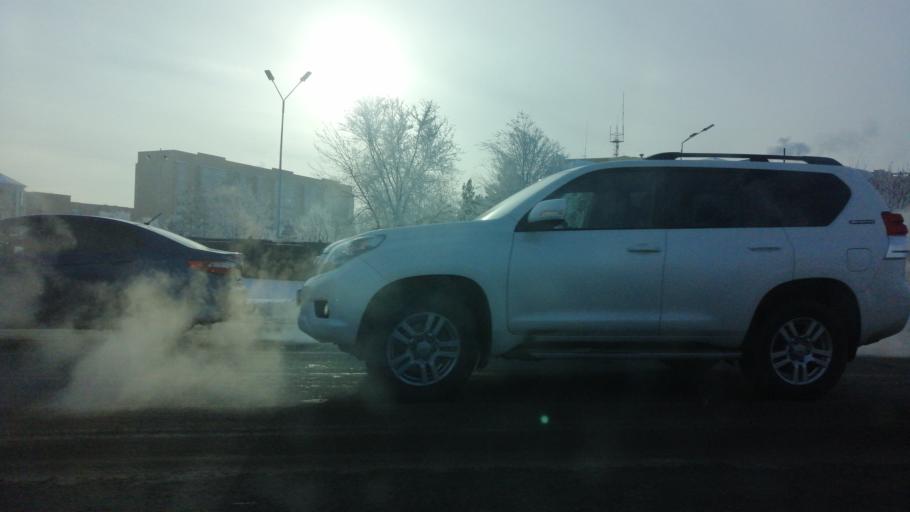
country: KZ
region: Aqtoebe
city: Aqtobe
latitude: 50.2836
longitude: 57.1377
